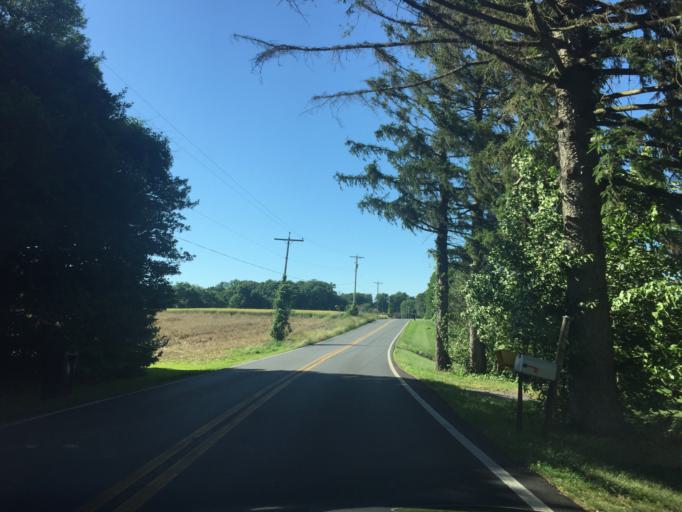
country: US
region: Maryland
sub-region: Carroll County
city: Westminster
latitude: 39.5826
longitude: -76.9283
